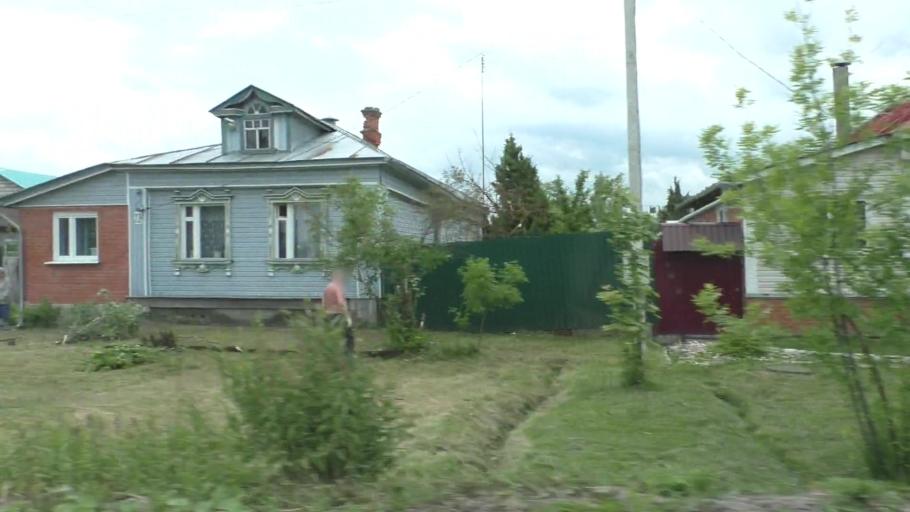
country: RU
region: Moskovskaya
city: Yegor'yevsk
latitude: 55.3994
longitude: 39.0101
